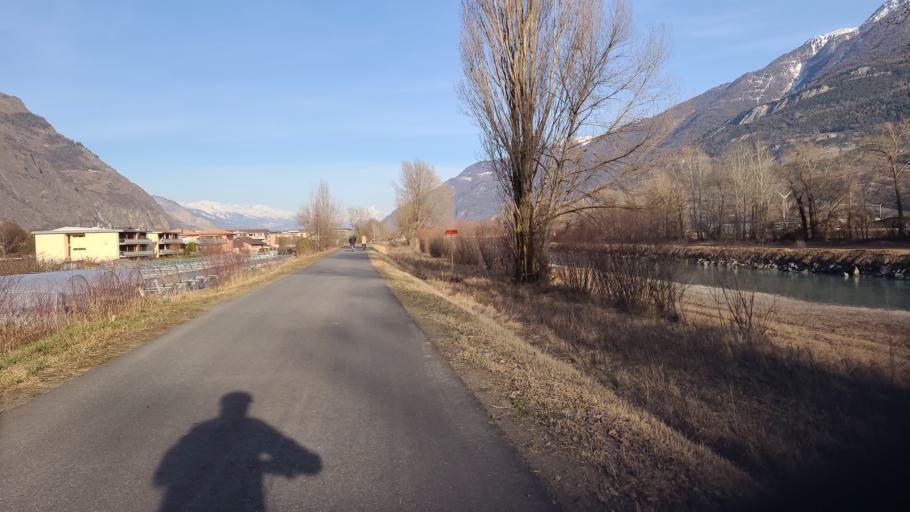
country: CH
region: Valais
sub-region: Martigny District
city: Fully
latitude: 46.1332
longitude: 7.1138
